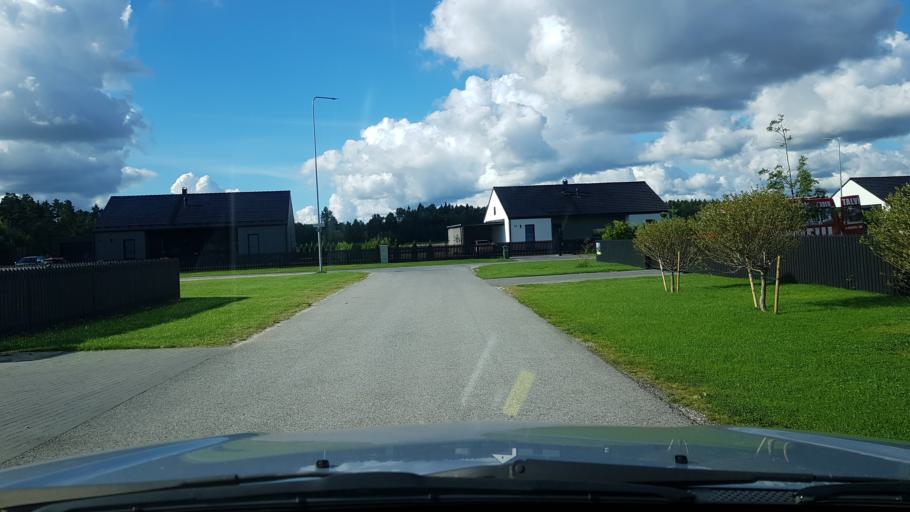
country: EE
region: Harju
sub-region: Kiili vald
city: Kiili
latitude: 59.3615
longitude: 24.8061
